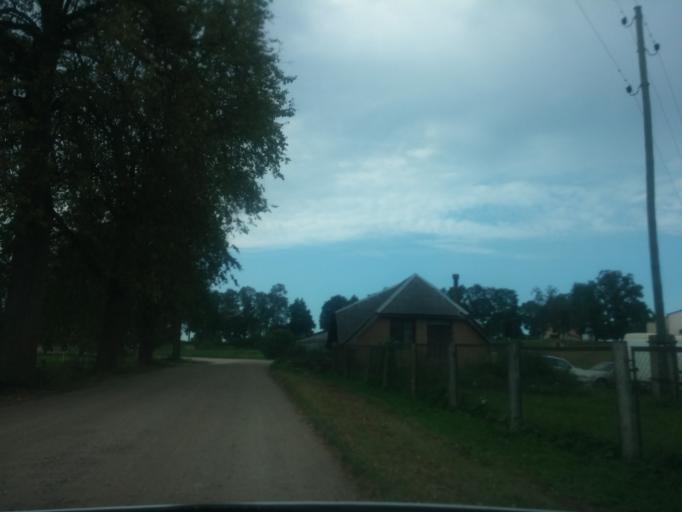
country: LV
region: Ogre
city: Ogre
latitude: 56.8661
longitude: 24.5716
